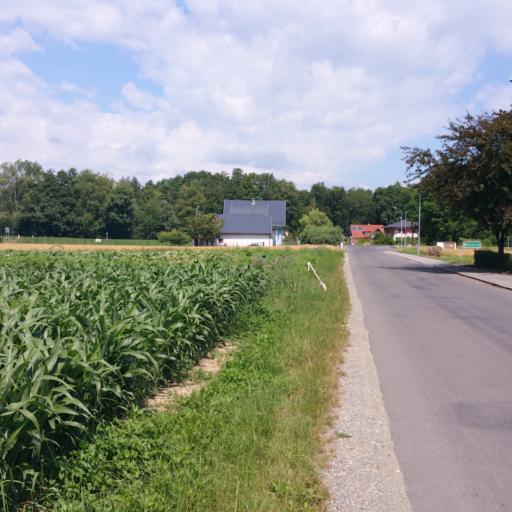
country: AT
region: Styria
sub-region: Politischer Bezirk Leibnitz
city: Gleinstatten
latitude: 46.7504
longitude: 15.3574
